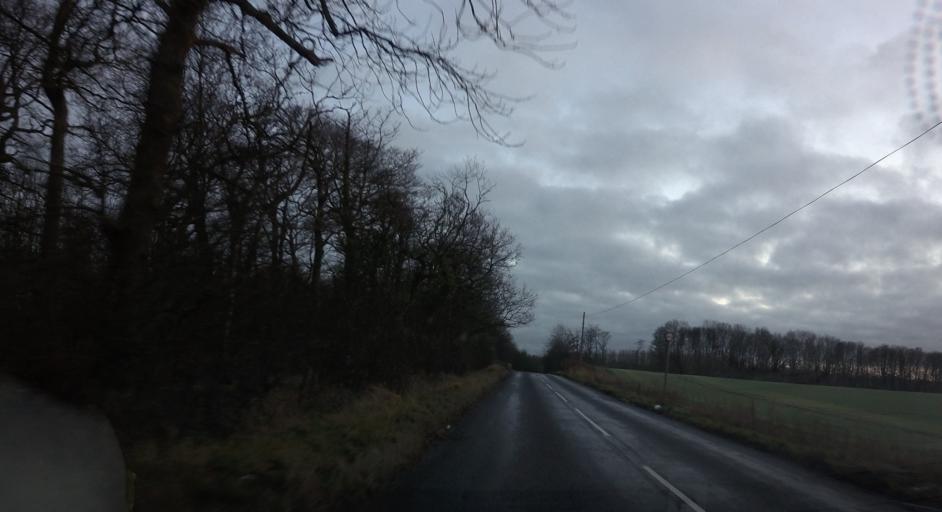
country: GB
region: Scotland
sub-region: Fife
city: Crossford
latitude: 56.0494
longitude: -3.4861
